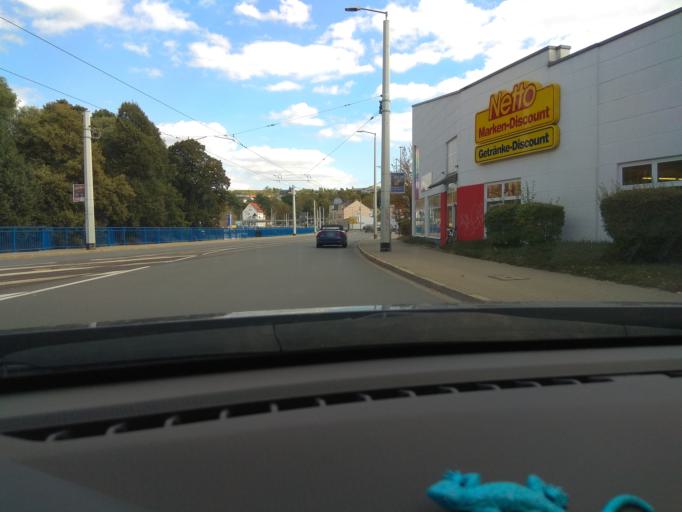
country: DE
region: Saxony
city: Plauen
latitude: 50.4925
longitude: 12.1430
